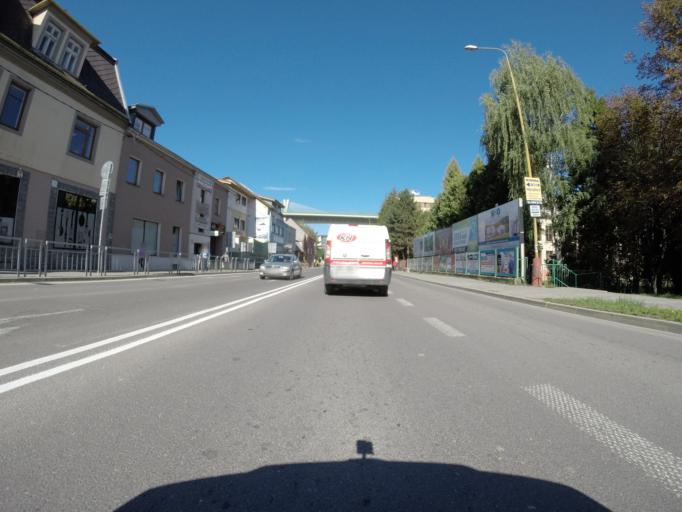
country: SK
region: Trenciansky
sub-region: Okres Povazska Bystrica
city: Povazska Bystrica
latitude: 49.1165
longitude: 18.4412
